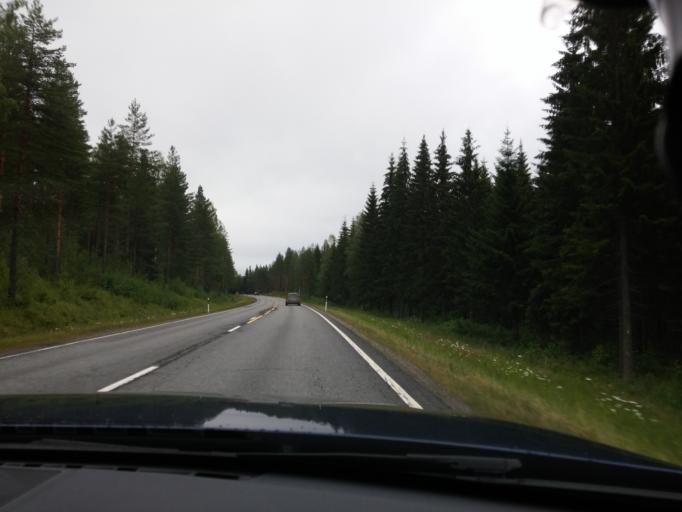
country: FI
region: Pirkanmaa
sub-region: Ylae-Pirkanmaa
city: Maenttae
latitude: 61.9599
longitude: 24.5861
